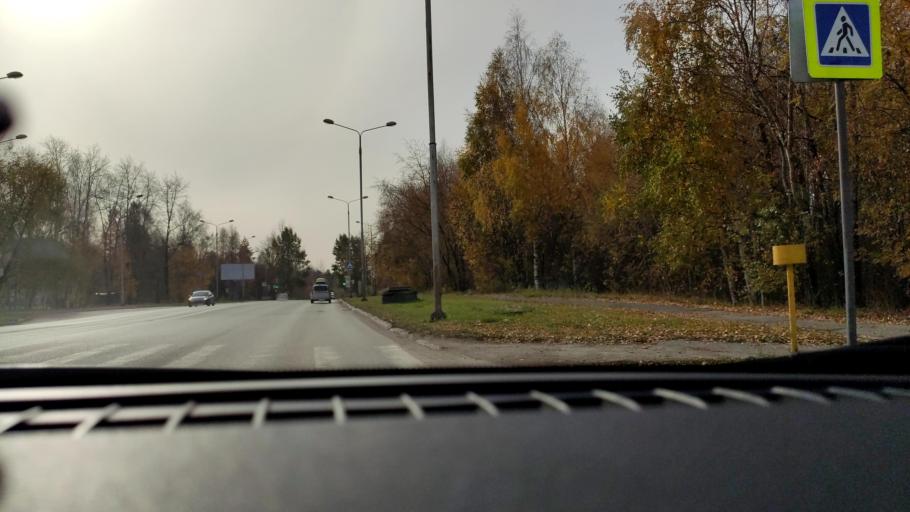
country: RU
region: Perm
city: Perm
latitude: 58.0928
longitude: 56.3832
